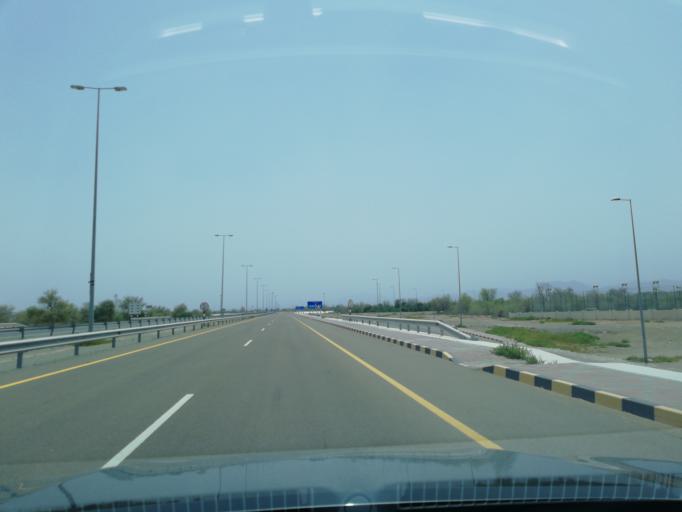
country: OM
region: Al Batinah
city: Shinas
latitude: 24.7493
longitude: 56.4622
